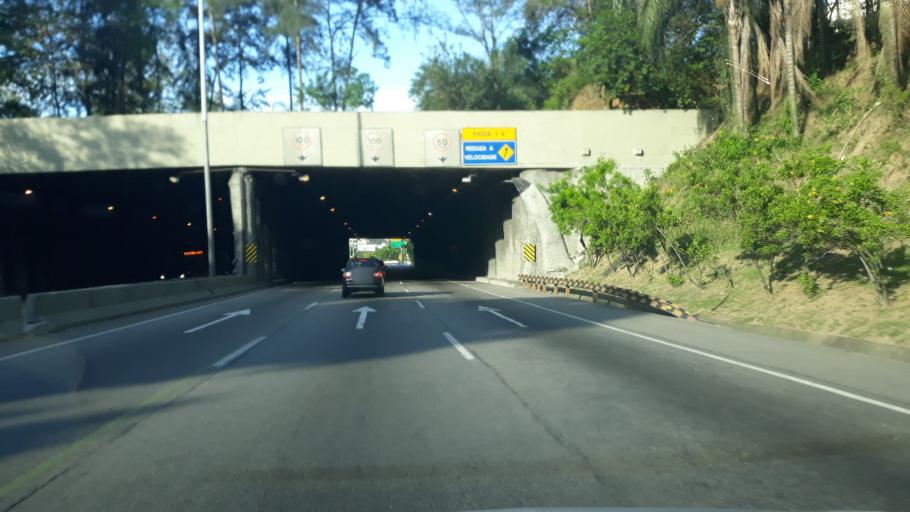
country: BR
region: Rio de Janeiro
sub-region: Sao Joao De Meriti
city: Sao Joao de Meriti
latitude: -22.9248
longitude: -43.3382
